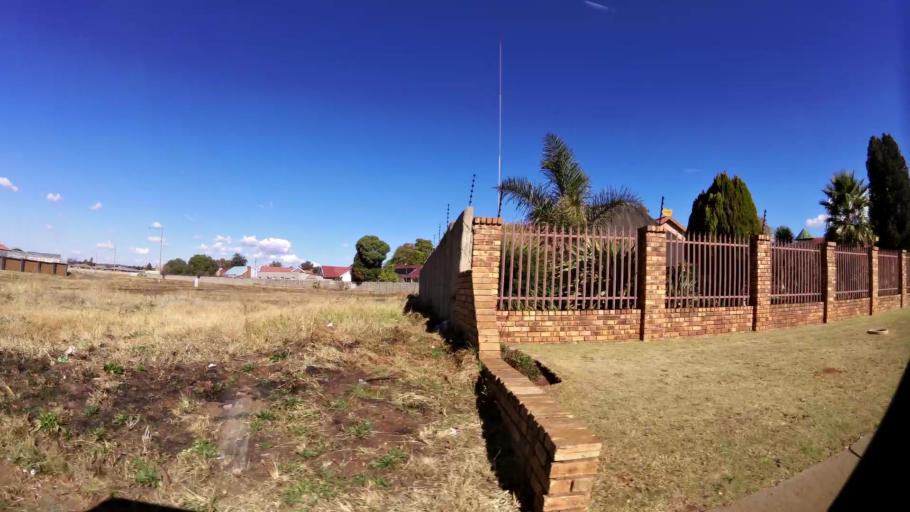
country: ZA
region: Gauteng
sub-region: West Rand District Municipality
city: Carletonville
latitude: -26.3583
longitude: 27.3713
